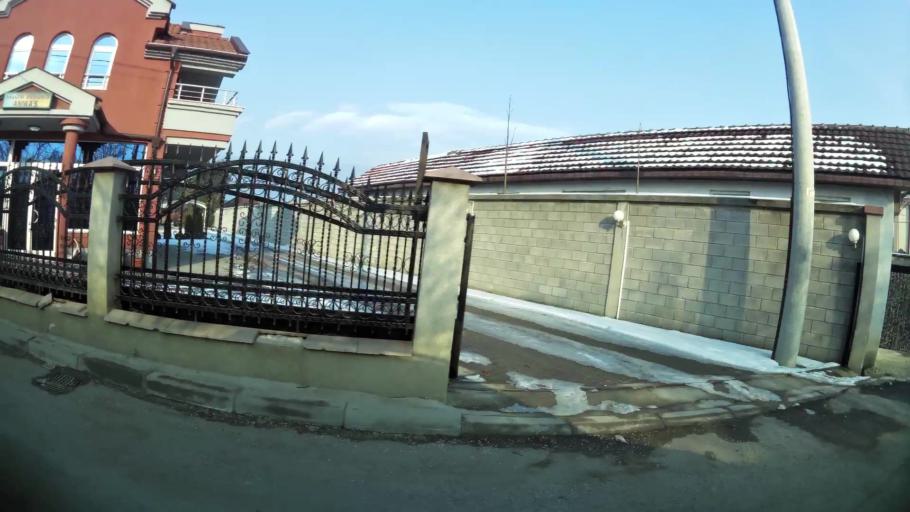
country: MK
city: Creshevo
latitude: 42.0204
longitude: 21.5104
